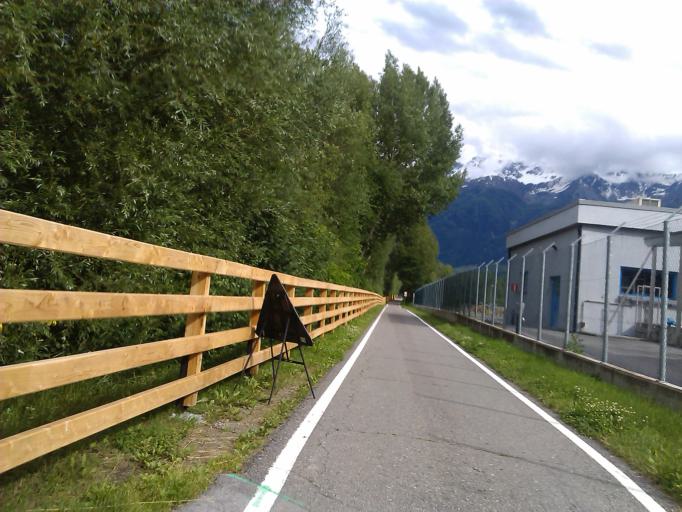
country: IT
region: Trentino-Alto Adige
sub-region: Bolzano
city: Glorenza
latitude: 46.6577
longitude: 10.5678
